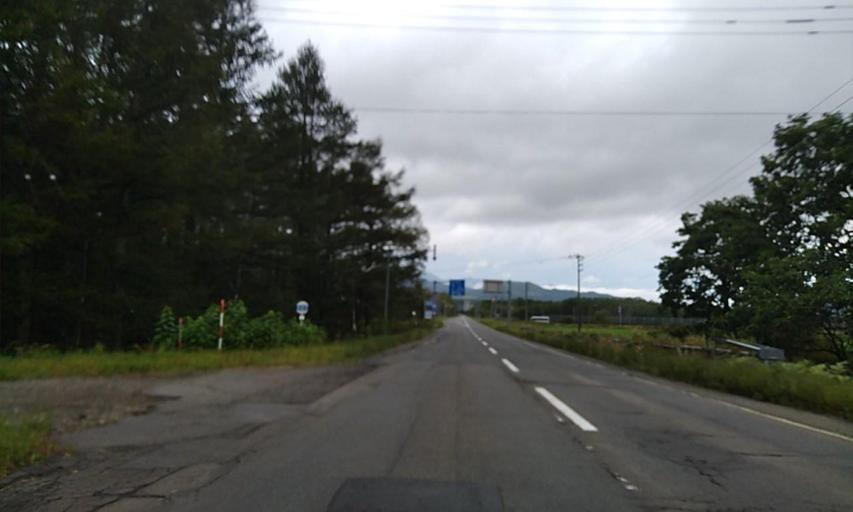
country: JP
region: Hokkaido
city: Bihoro
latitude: 43.5151
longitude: 144.4332
